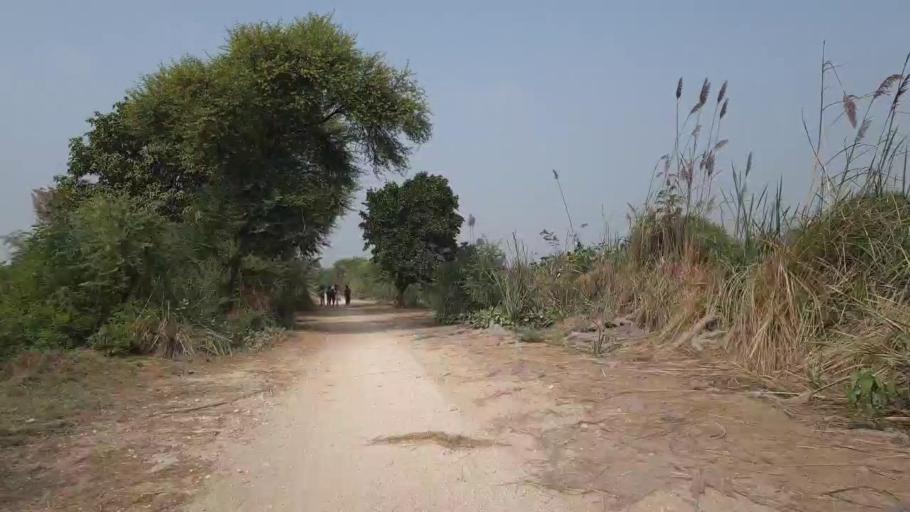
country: PK
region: Sindh
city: Matli
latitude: 25.0236
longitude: 68.5975
